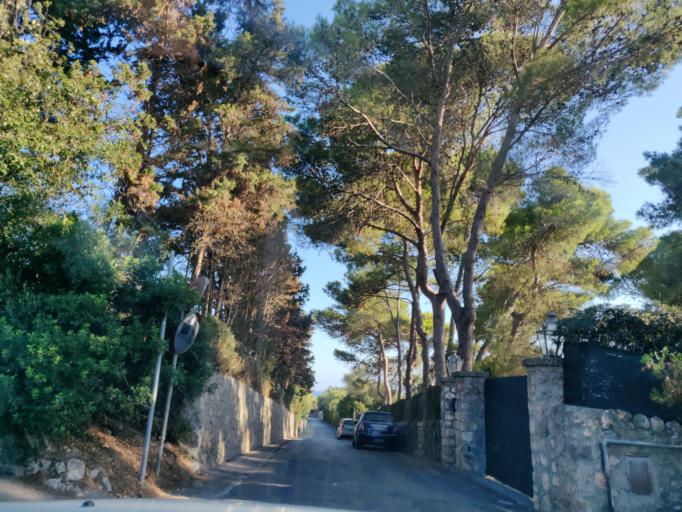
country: IT
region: Tuscany
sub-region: Provincia di Grosseto
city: Orbetello Scalo
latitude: 42.4110
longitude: 11.2807
